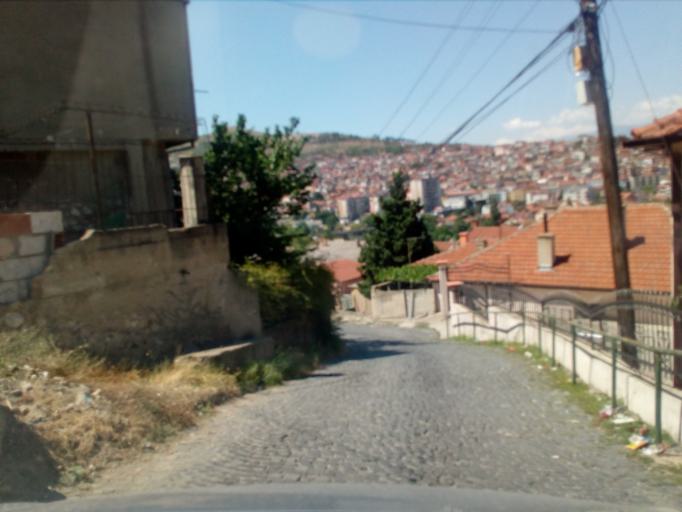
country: MK
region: Veles
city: Veles
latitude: 41.7186
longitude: 21.7894
